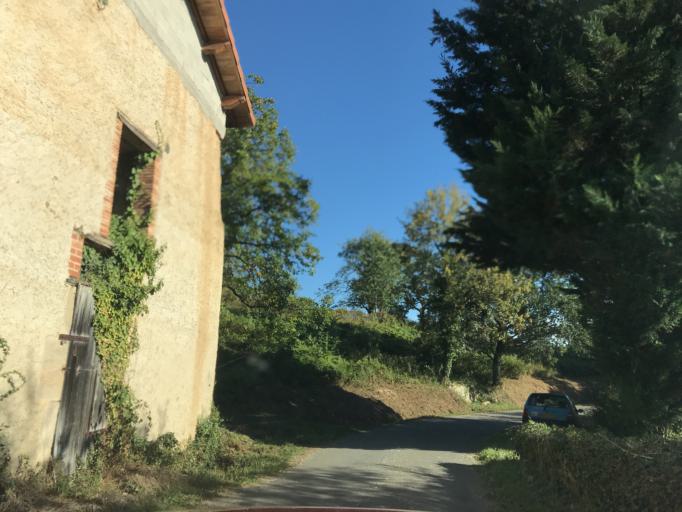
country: FR
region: Auvergne
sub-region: Departement du Puy-de-Dome
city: Escoutoux
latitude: 45.7694
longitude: 3.6258
